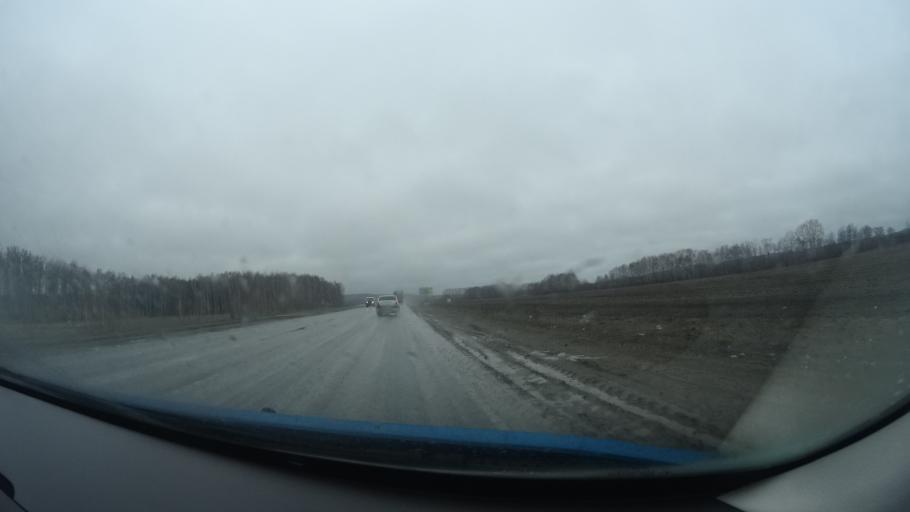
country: RU
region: Bashkortostan
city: Kandry
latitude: 54.6101
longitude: 54.3141
